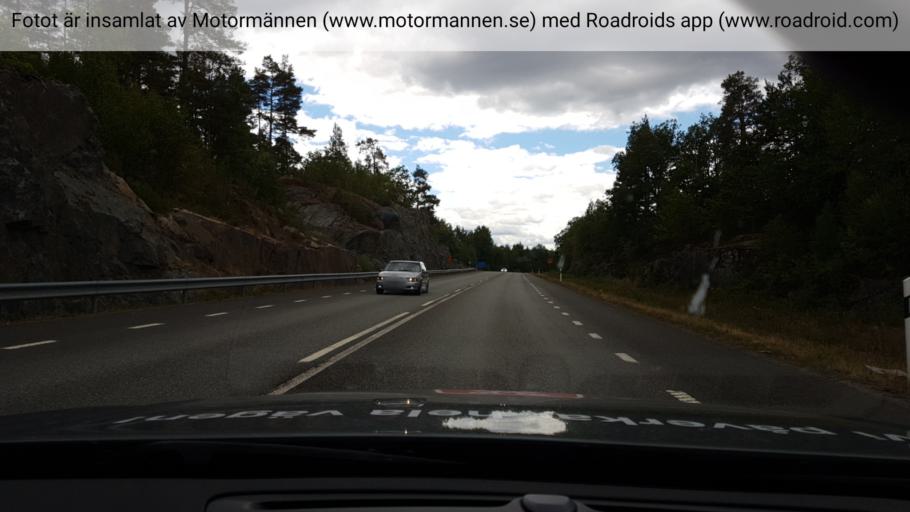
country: SE
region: Kalmar
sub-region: Vasterviks Kommun
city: Ankarsrum
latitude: 57.6599
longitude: 16.4448
